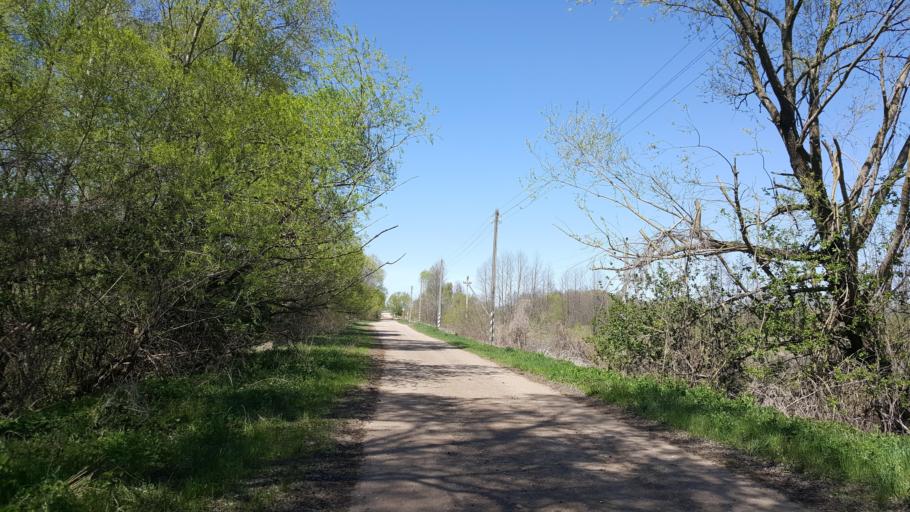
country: BY
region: Brest
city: Charnawchytsy
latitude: 52.3260
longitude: 23.6558
